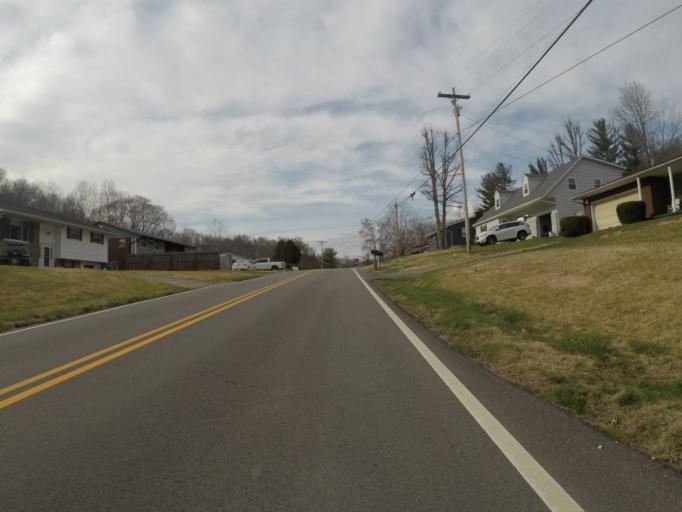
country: US
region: Ohio
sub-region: Lawrence County
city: Burlington
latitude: 38.4375
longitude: -82.4972
